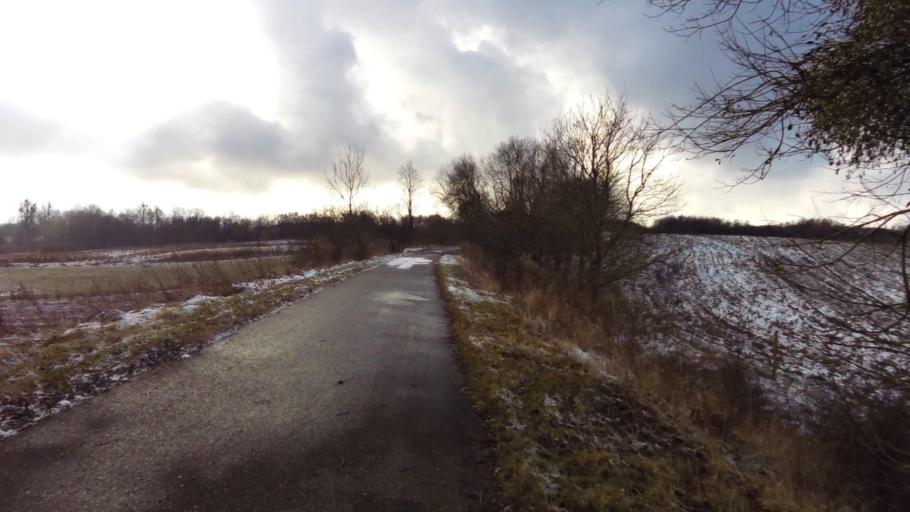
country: PL
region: West Pomeranian Voivodeship
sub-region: Powiat swidwinski
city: Polczyn-Zdroj
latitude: 53.7618
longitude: 16.0680
